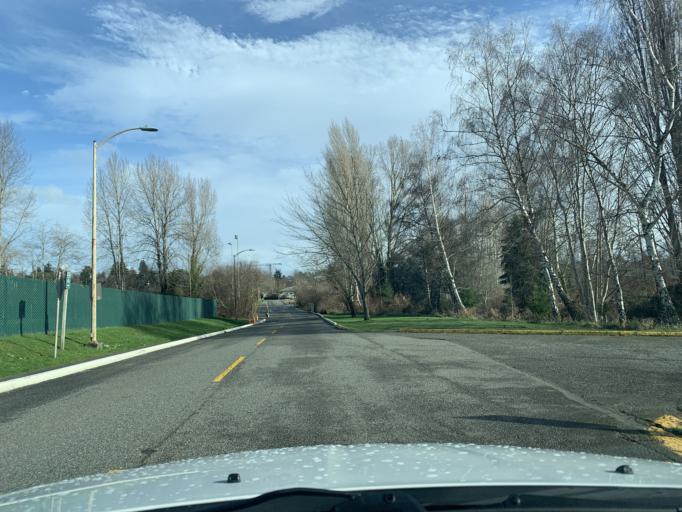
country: US
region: Washington
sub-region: King County
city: Seattle
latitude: 47.6586
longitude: -122.2970
